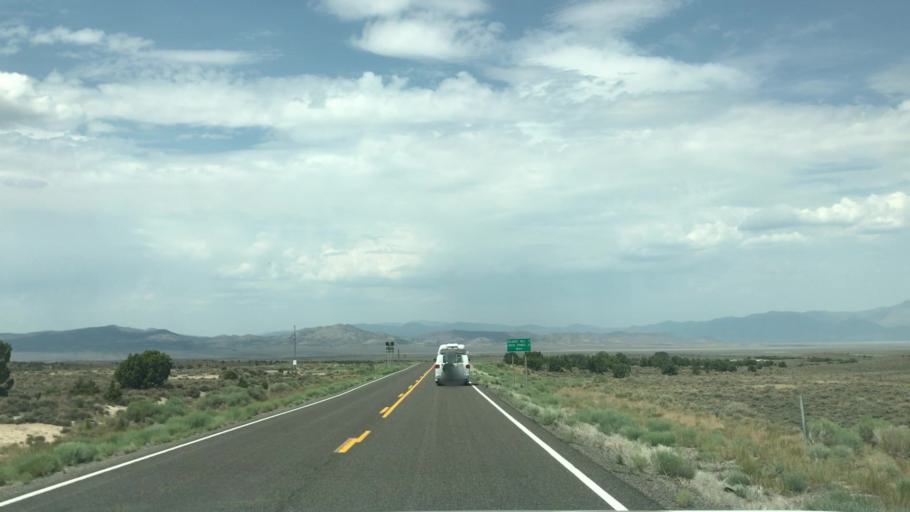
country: US
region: Nevada
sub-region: Eureka County
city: Eureka
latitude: 39.3939
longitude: -115.5228
